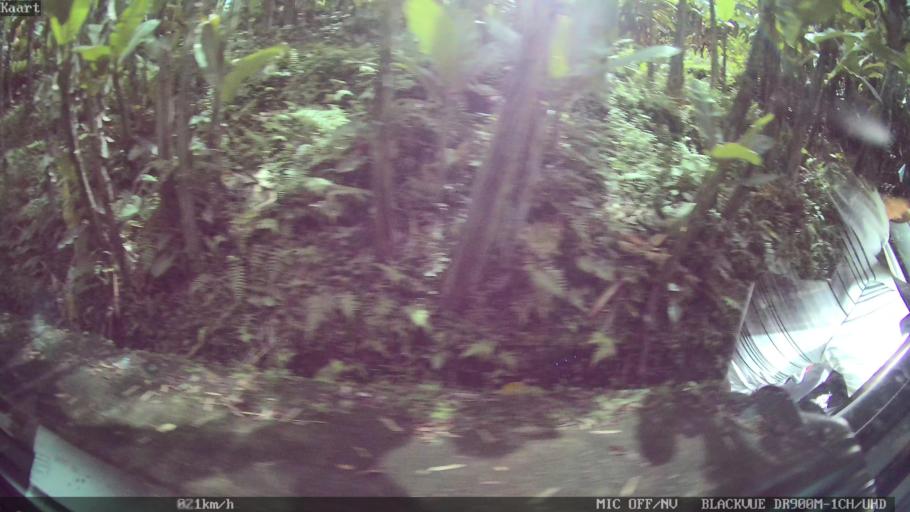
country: ID
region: Bali
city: Pemijian
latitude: -8.4414
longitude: 115.2261
